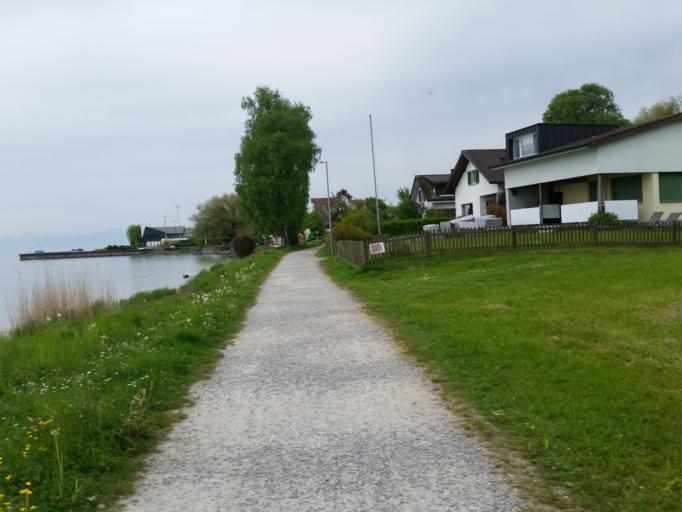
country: CH
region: Thurgau
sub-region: Arbon District
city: Uttwil
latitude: 47.5986
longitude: 9.3175
